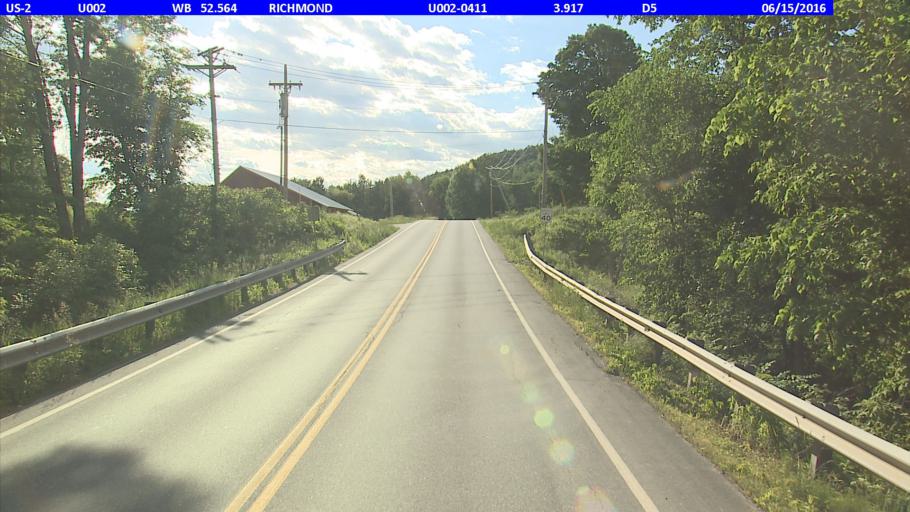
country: US
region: Vermont
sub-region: Chittenden County
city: Williston
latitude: 44.4006
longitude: -72.9735
